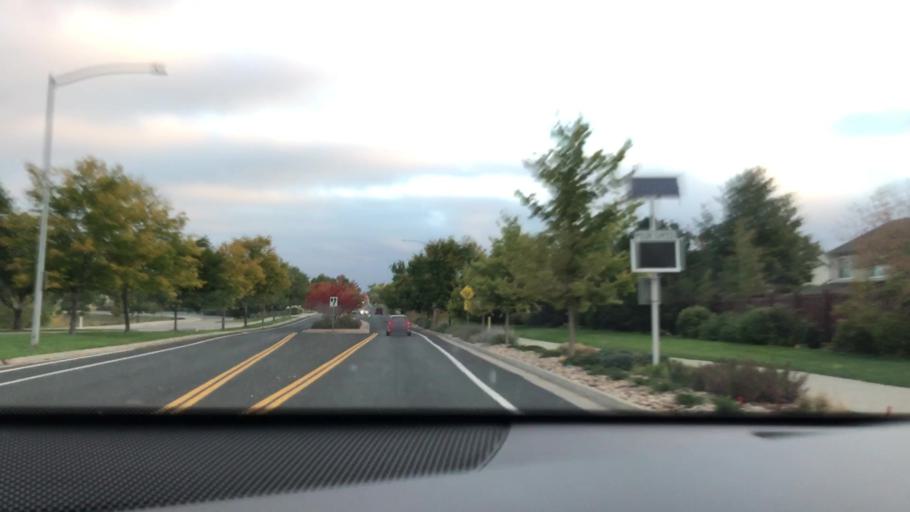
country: US
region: Colorado
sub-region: Broomfield County
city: Broomfield
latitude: 39.9470
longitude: -105.0624
